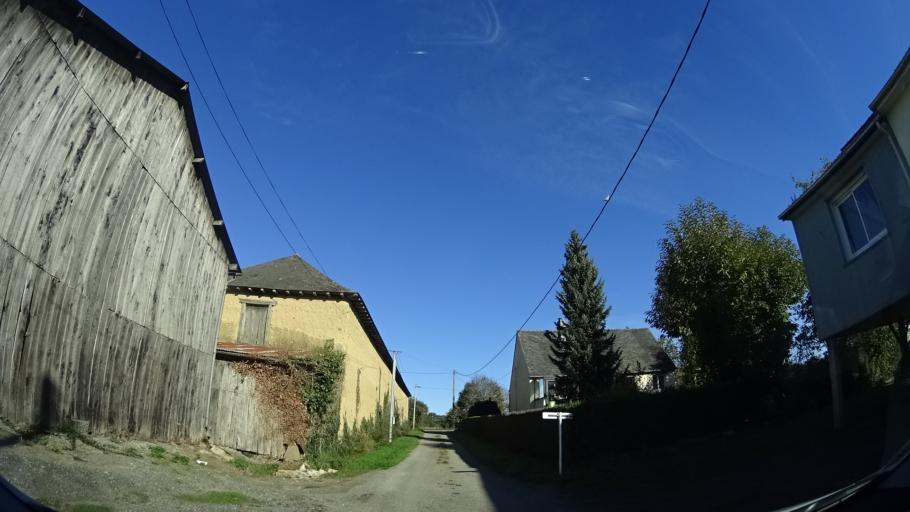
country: FR
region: Brittany
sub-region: Departement d'Ille-et-Vilaine
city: La Meziere
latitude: 48.2094
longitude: -1.7648
